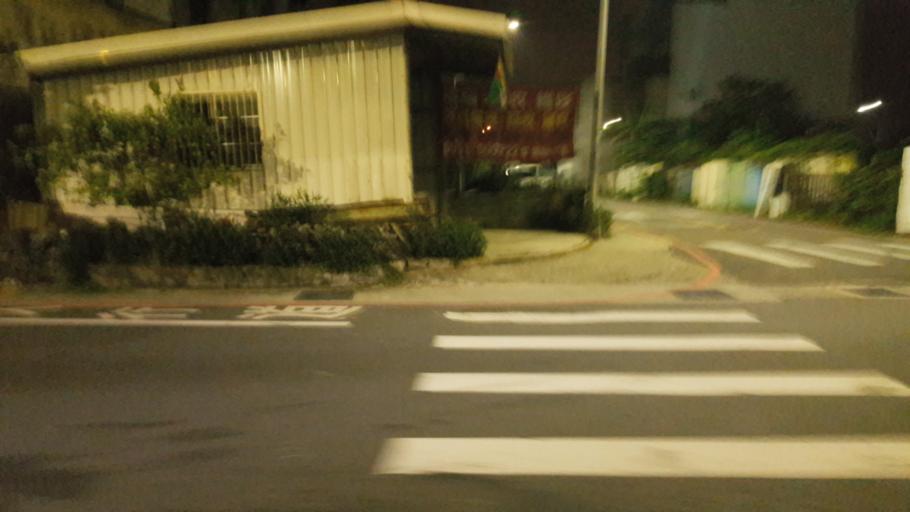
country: TW
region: Taiwan
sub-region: Hsinchu
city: Hsinchu
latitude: 24.7677
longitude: 120.9788
